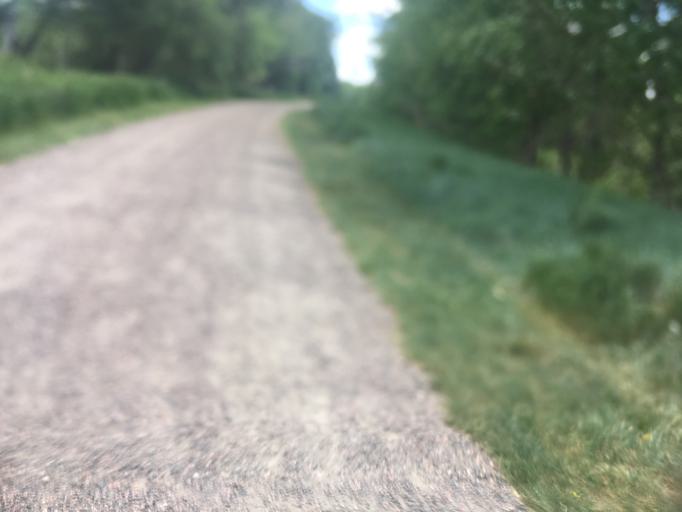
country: US
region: Colorado
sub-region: Boulder County
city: Lafayette
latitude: 39.9989
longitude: -105.1148
